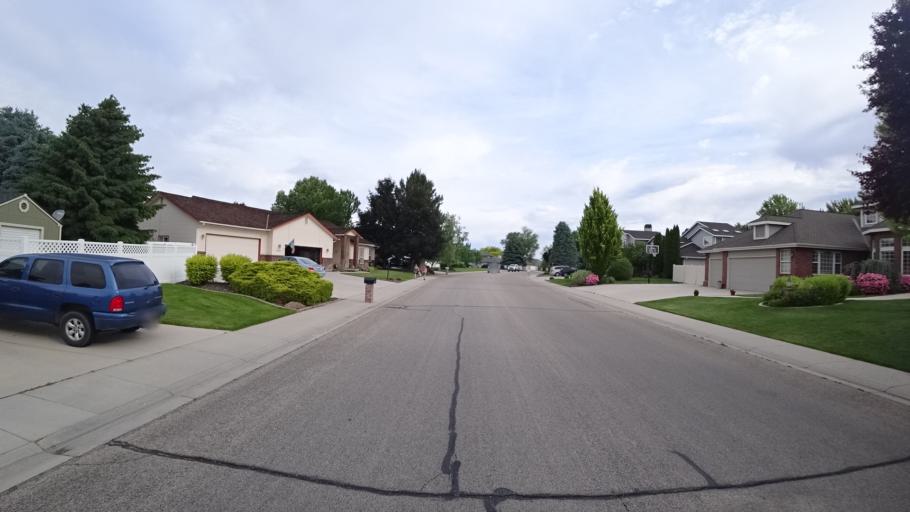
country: US
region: Idaho
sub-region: Ada County
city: Meridian
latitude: 43.5870
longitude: -116.3853
